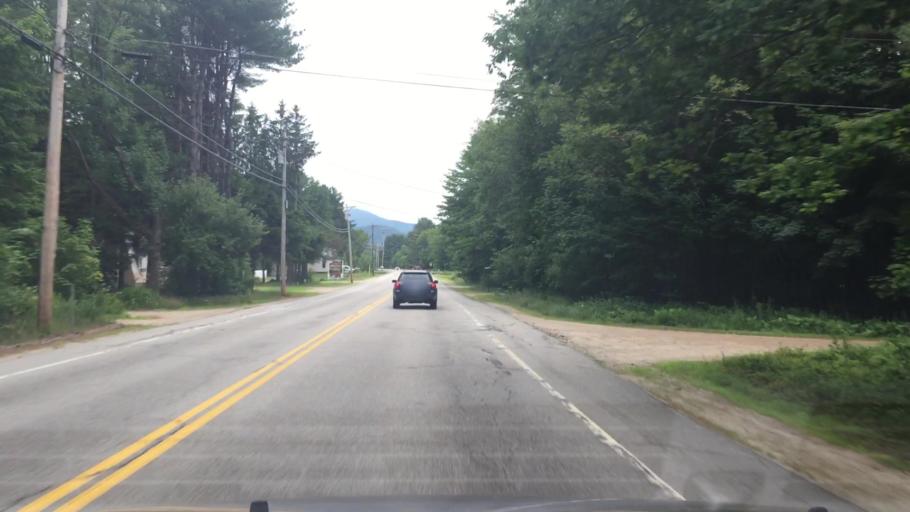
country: US
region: New Hampshire
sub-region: Carroll County
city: North Conway
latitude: 44.0789
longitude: -71.2639
